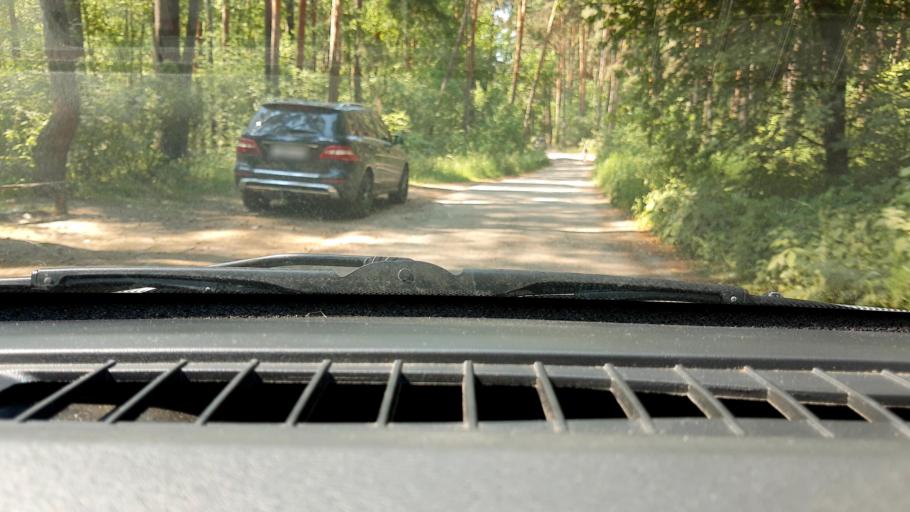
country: RU
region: Nizjnij Novgorod
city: Burevestnik
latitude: 56.1945
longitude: 43.7891
